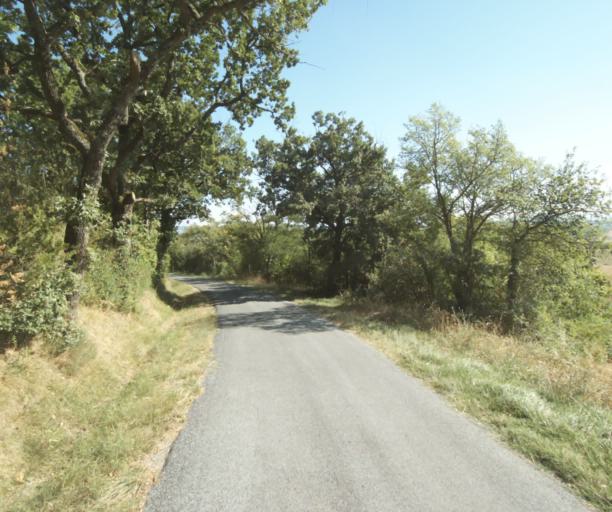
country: FR
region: Midi-Pyrenees
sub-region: Departement de la Haute-Garonne
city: Saint-Felix-Lauragais
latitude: 43.5204
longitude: 1.9137
